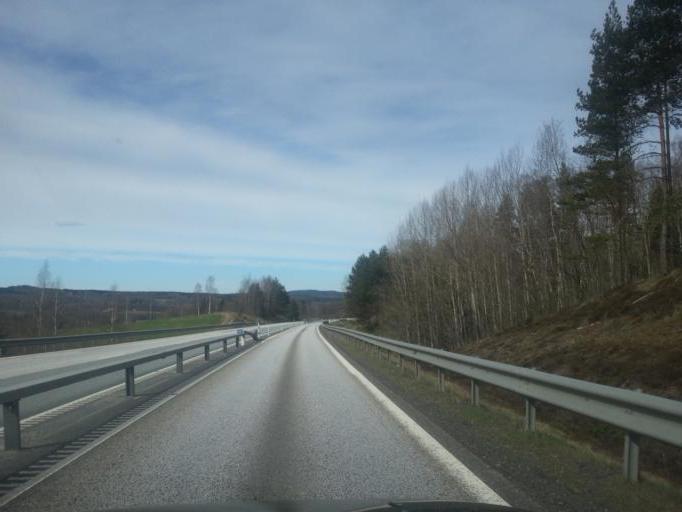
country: SE
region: Joenkoeping
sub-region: Jonkopings Kommun
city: Bankeryd
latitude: 57.7990
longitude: 14.0973
